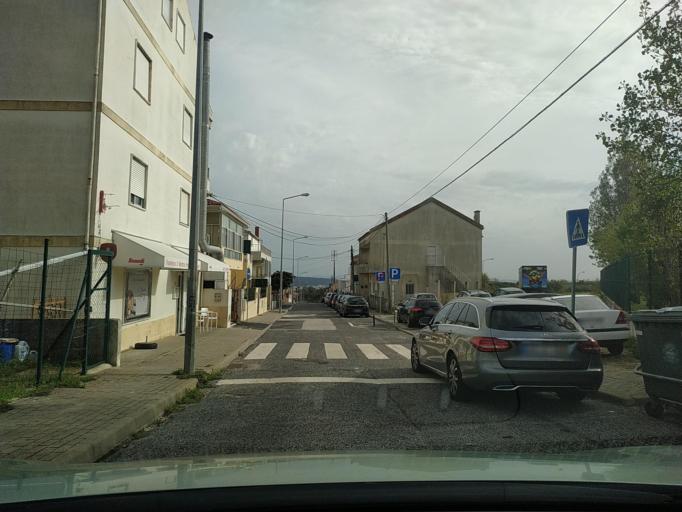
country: PT
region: Lisbon
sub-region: Sintra
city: Belas
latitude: 38.7755
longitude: -9.2394
